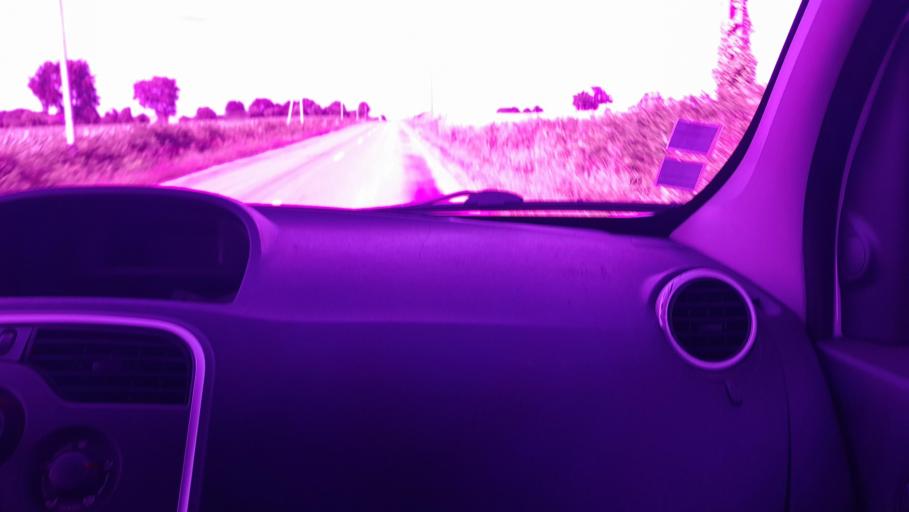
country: FR
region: Pays de la Loire
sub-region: Departement de la Mayenne
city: Ballots
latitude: 47.9501
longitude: -1.0706
